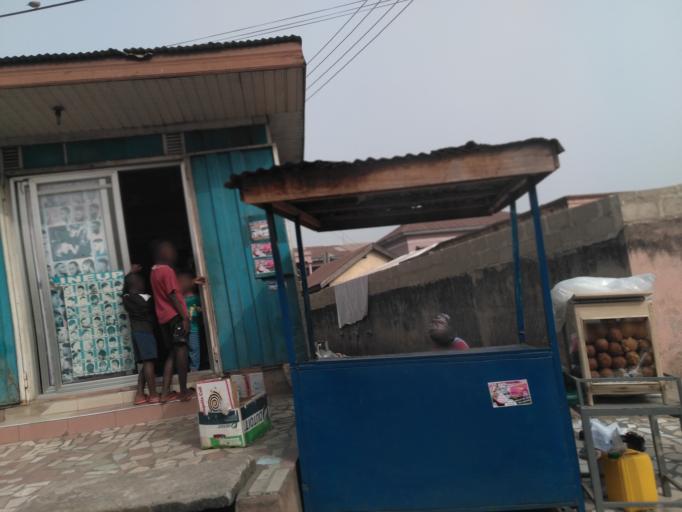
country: GH
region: Ashanti
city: Kumasi
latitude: 6.6983
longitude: -1.6087
